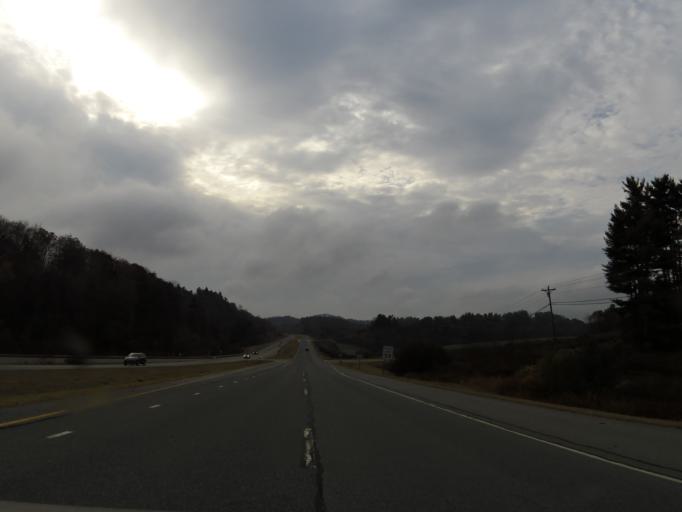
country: US
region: North Carolina
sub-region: Watauga County
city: Boone
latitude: 36.2357
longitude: -81.5600
